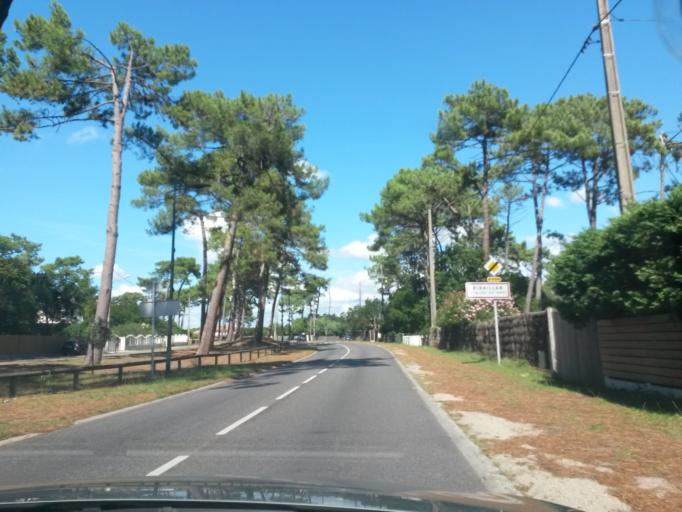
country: FR
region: Aquitaine
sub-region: Departement de la Gironde
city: Arcachon
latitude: 44.7051
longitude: -1.2256
